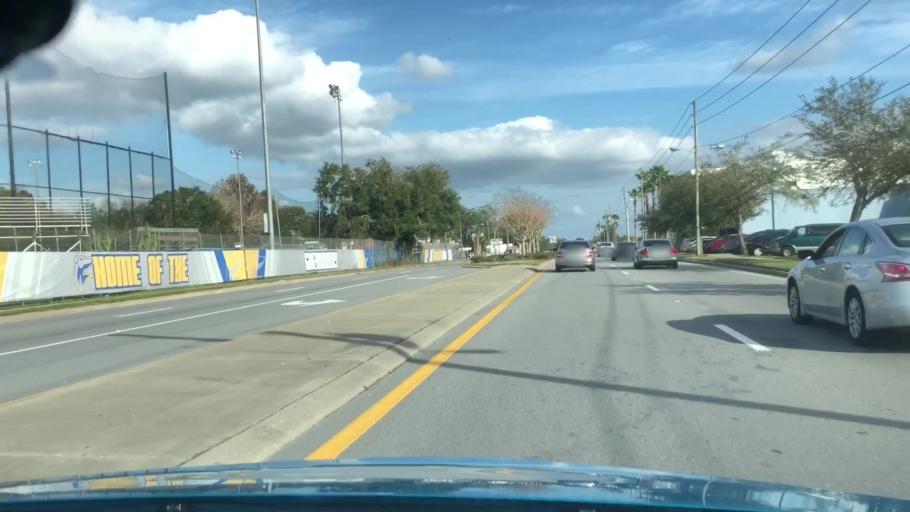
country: US
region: Florida
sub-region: Seminole County
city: Casselberry
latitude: 28.6849
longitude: -81.3434
